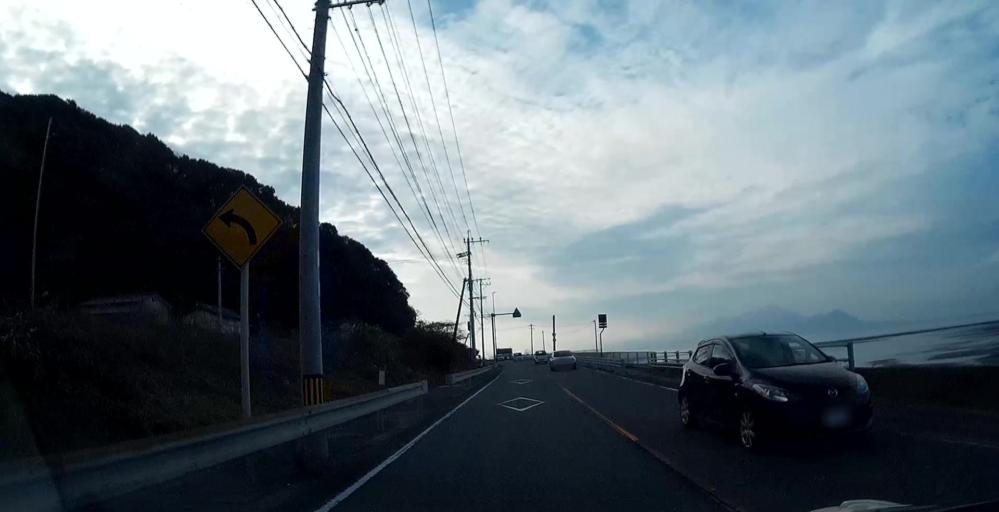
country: JP
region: Kumamoto
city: Matsubase
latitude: 32.6647
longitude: 130.5366
